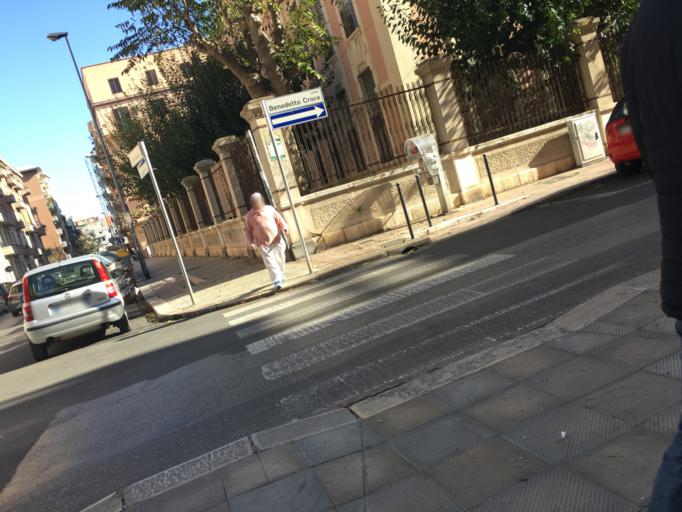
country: IT
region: Apulia
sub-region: Provincia di Bari
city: Bari
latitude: 41.1119
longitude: 16.8715
